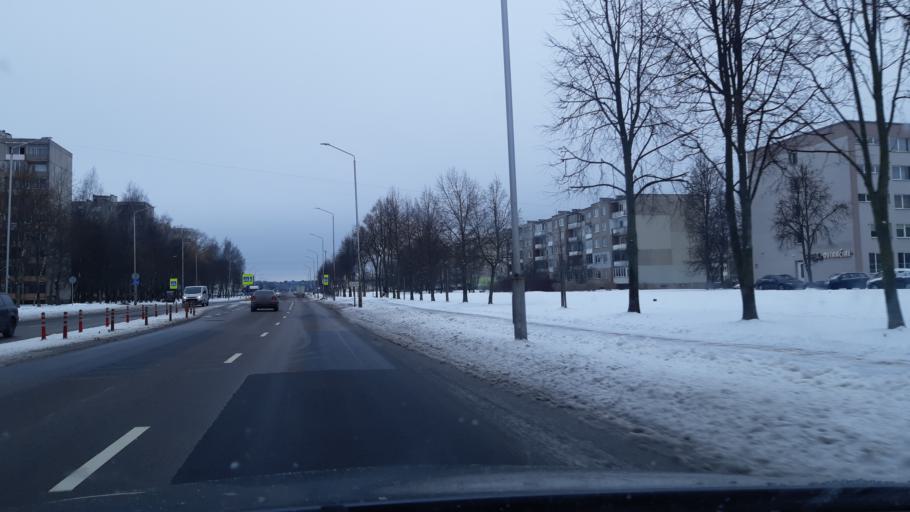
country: LT
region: Kauno apskritis
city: Dainava (Kaunas)
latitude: 54.9243
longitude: 23.9778
